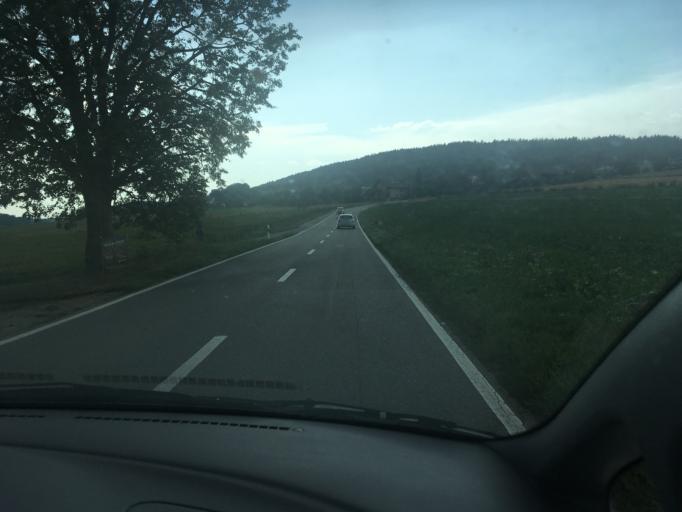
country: CH
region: Bern
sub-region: Seeland District
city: Schupfen
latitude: 47.0090
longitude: 7.3733
